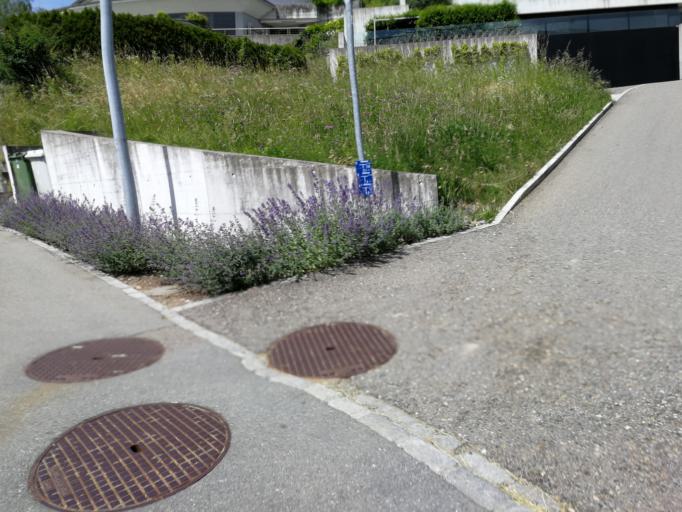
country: CH
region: Saint Gallen
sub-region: Wahlkreis See-Gaster
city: Rapperswil
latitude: 47.2437
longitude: 8.8203
